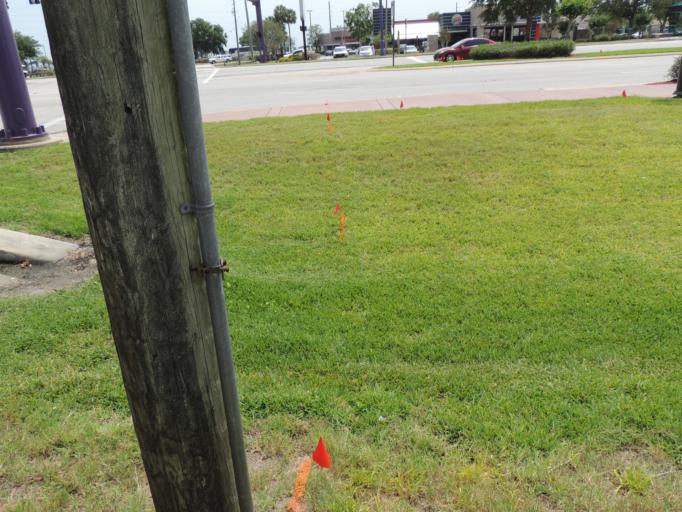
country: US
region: Florida
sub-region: Osceola County
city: Celebration
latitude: 28.3353
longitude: -81.4800
